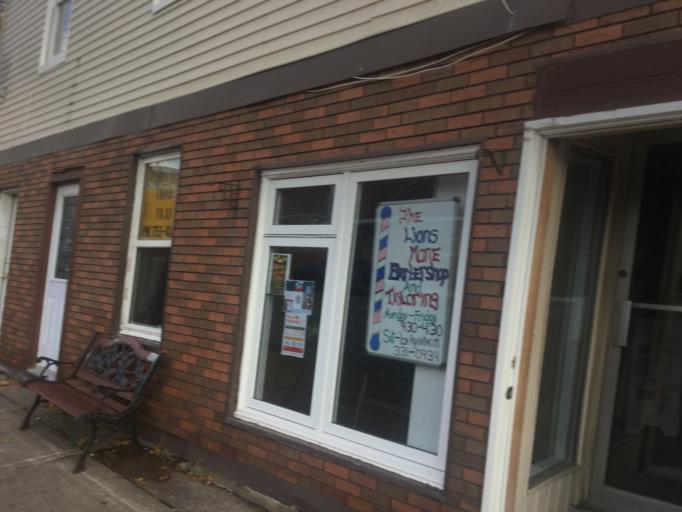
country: CA
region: Nova Scotia
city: New Glasgow
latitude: 45.5584
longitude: -62.6600
